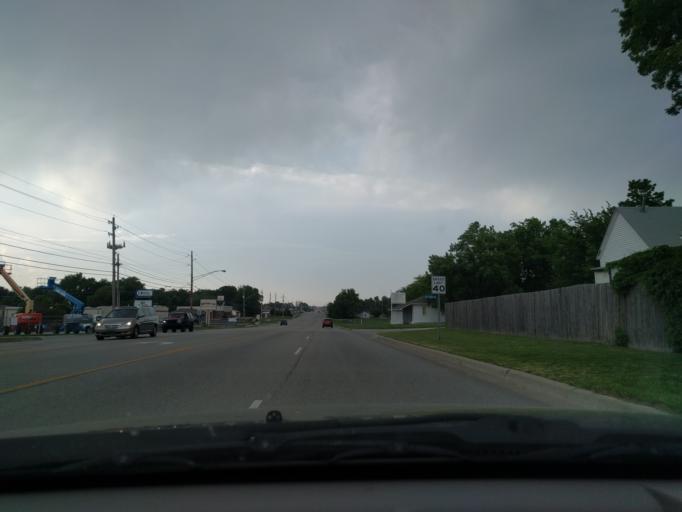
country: US
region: Oklahoma
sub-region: Tulsa County
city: Broken Arrow
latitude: 36.0550
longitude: -95.7974
